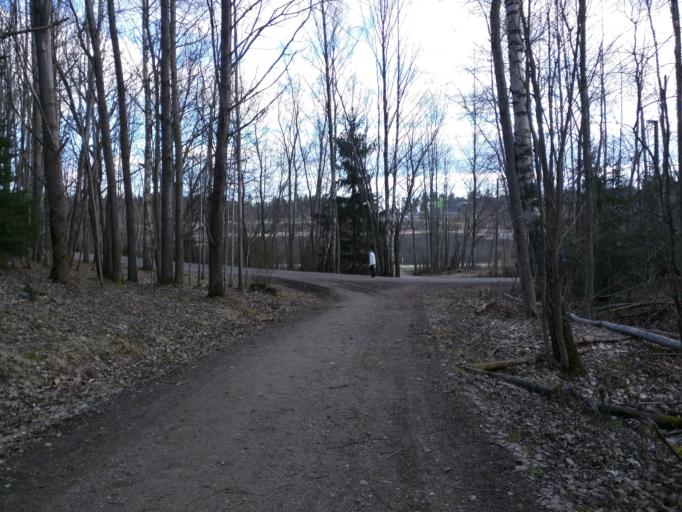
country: FI
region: Uusimaa
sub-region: Helsinki
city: Kilo
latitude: 60.2288
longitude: 24.7884
